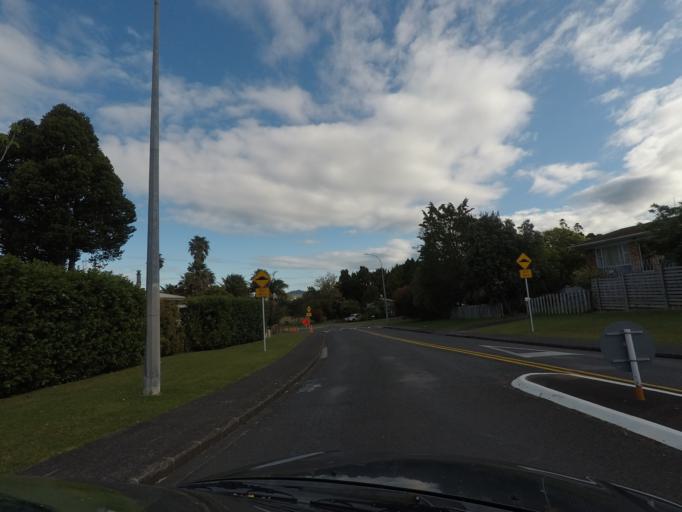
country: NZ
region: Auckland
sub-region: Auckland
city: Rosebank
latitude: -36.8852
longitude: 174.6487
